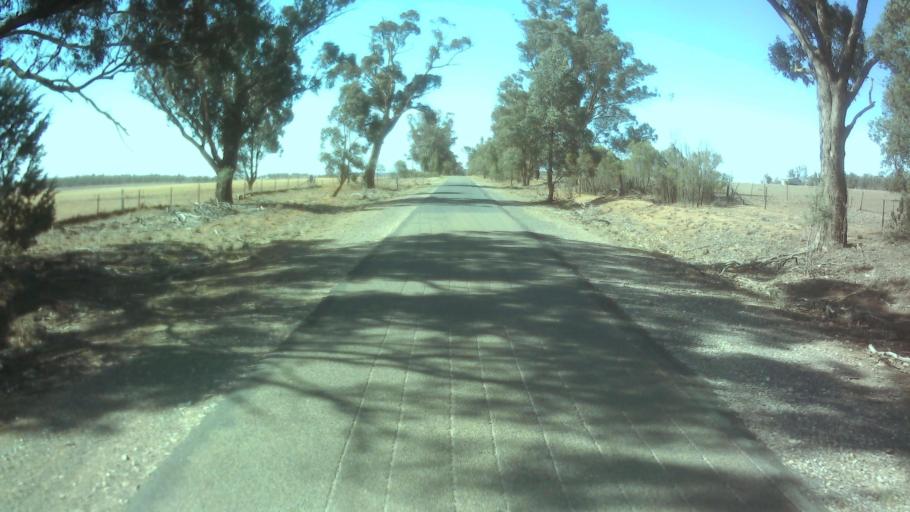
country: AU
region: New South Wales
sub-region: Forbes
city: Forbes
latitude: -33.7296
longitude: 147.7434
